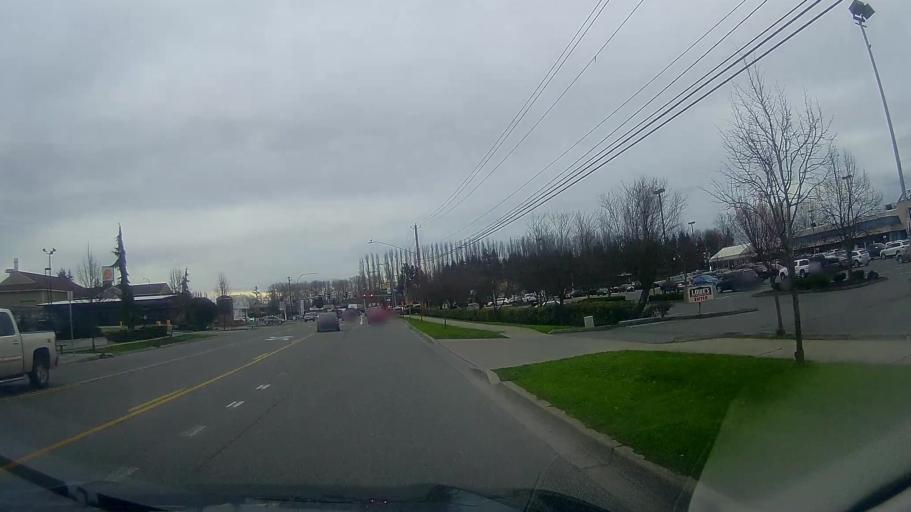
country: US
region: Washington
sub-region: Skagit County
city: Mount Vernon
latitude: 48.4377
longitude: -122.3432
